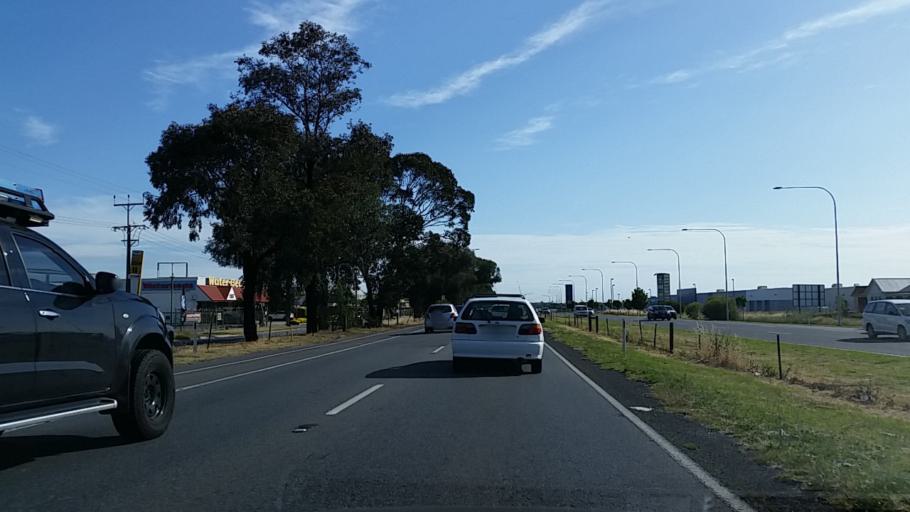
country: AU
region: South Australia
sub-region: Salisbury
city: Salisbury
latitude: -34.7966
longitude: 138.6427
